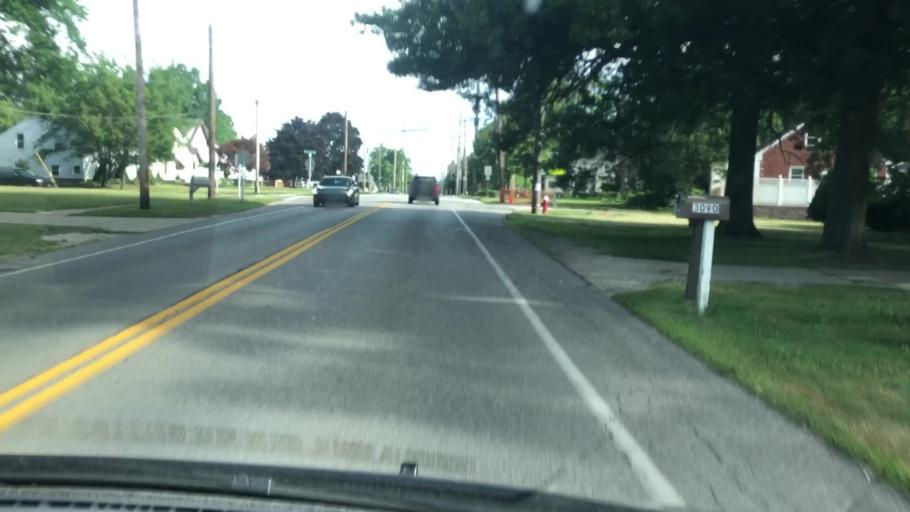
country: US
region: Ohio
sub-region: Summit County
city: Silver Lake
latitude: 41.1546
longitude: -81.4753
